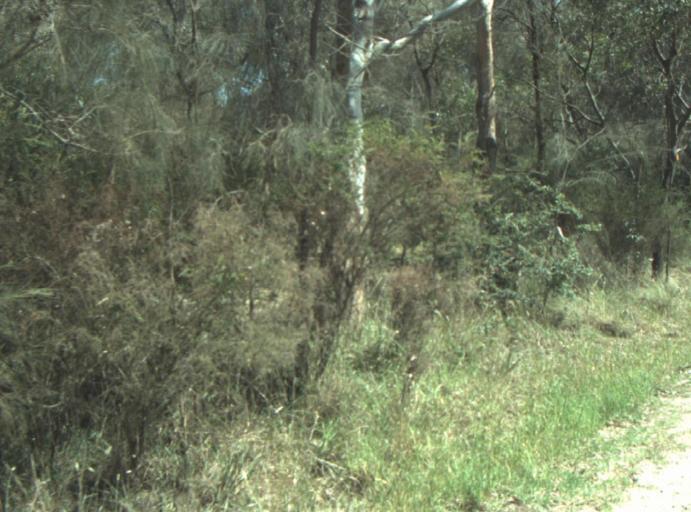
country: AU
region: Victoria
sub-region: Greater Geelong
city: Breakwater
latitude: -38.2420
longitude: 144.3524
